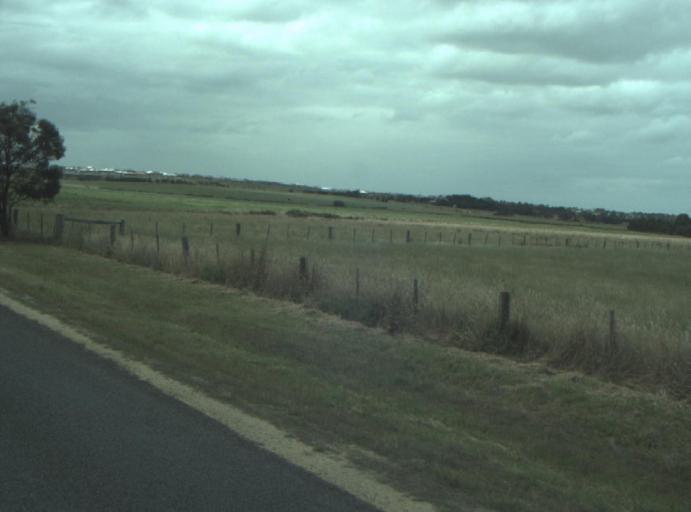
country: AU
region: Victoria
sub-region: Greater Geelong
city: Wandana Heights
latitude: -38.2250
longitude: 144.2993
